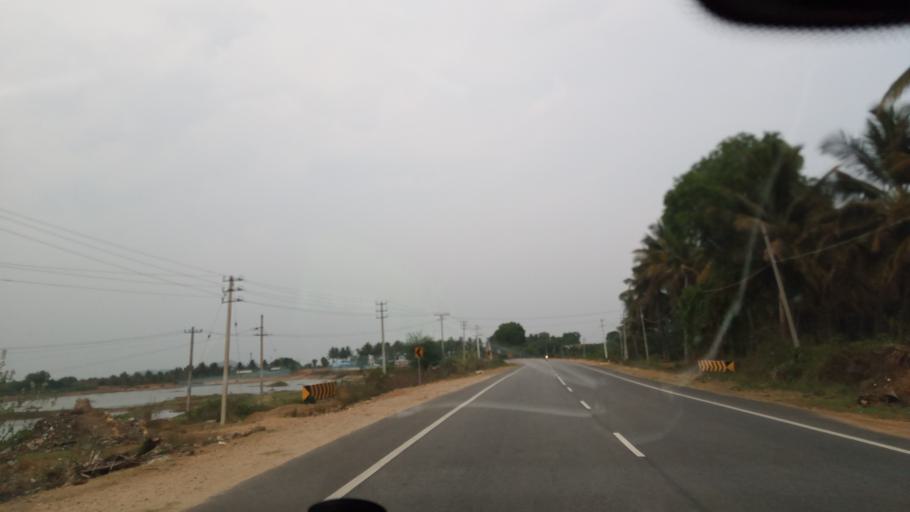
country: IN
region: Karnataka
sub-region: Mandya
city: Nagamangala
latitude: 12.7395
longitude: 76.7237
